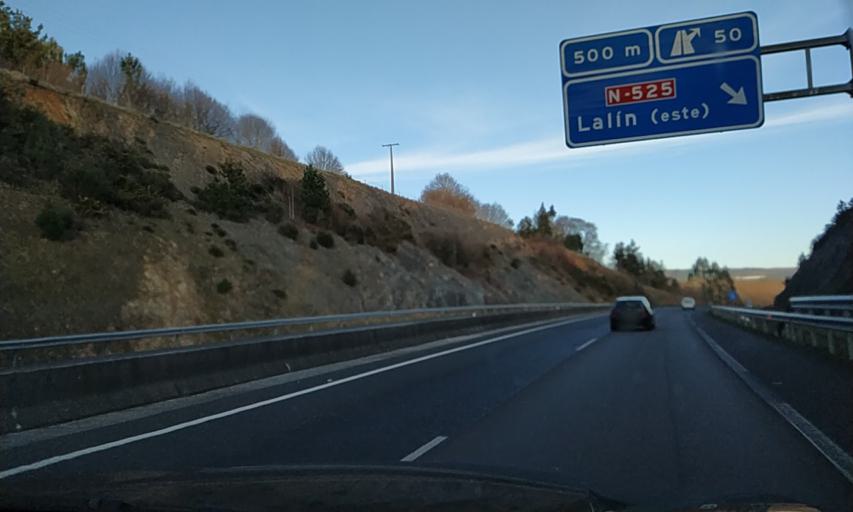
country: ES
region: Galicia
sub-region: Provincia de Pontevedra
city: Lalin
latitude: 42.6248
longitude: -8.1090
